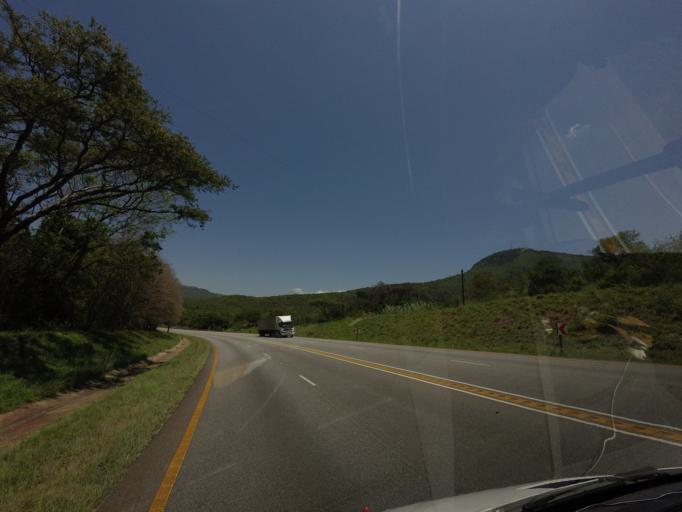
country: ZA
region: Mpumalanga
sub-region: Ehlanzeni District
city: Nelspruit
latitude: -25.4217
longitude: 30.7676
